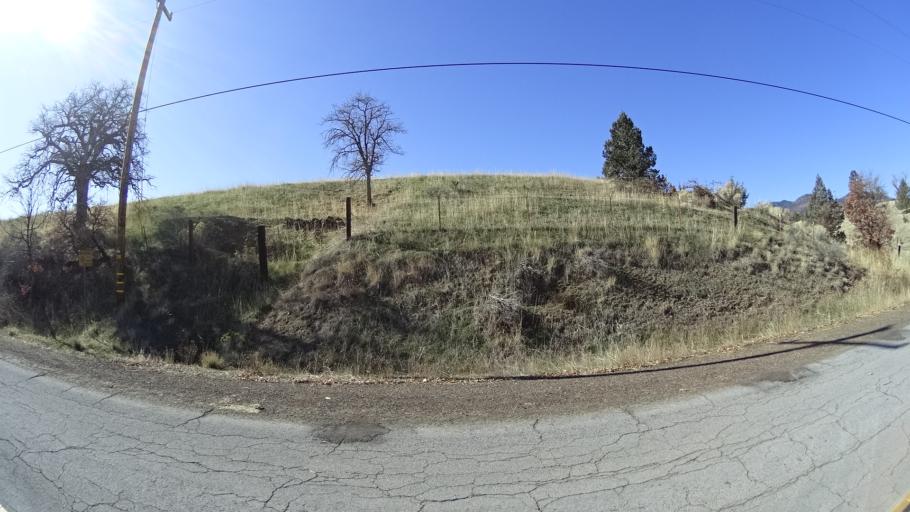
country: US
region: California
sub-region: Siskiyou County
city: Montague
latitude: 41.9126
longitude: -122.5619
